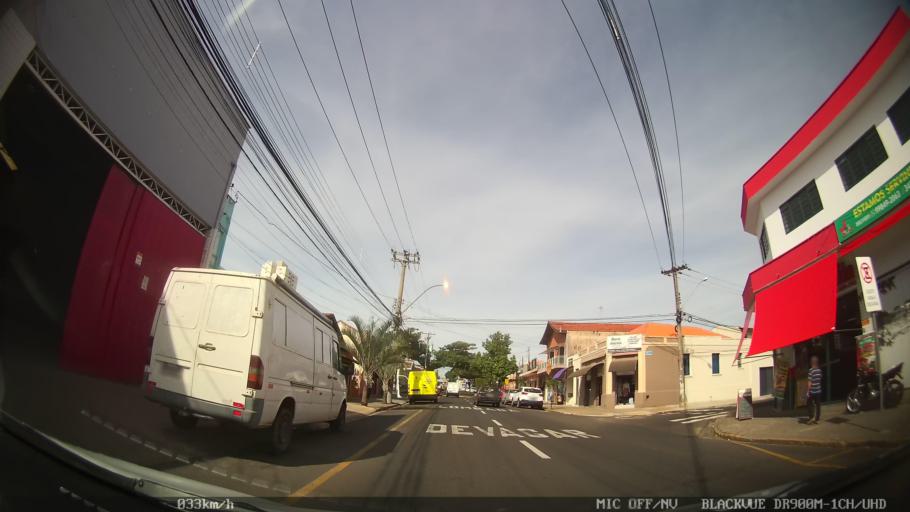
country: BR
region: Sao Paulo
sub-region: Piracicaba
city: Piracicaba
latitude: -22.7476
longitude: -47.6501
